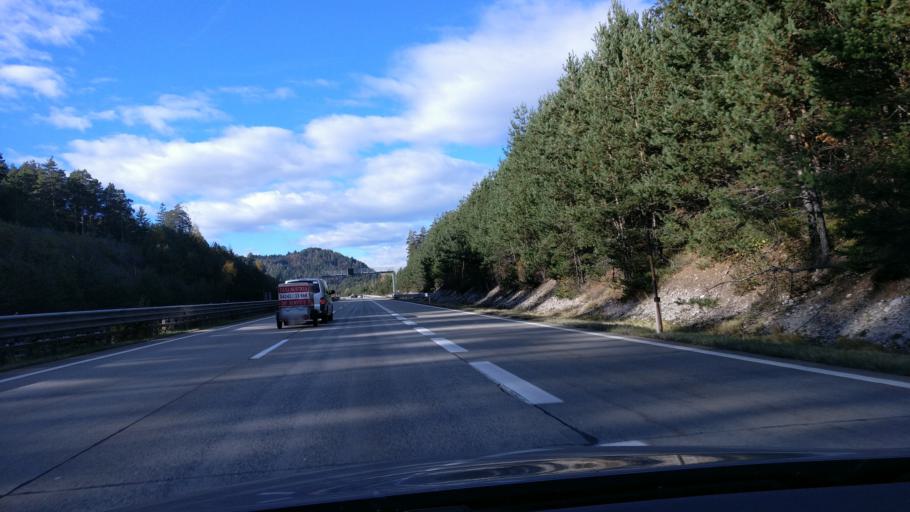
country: AT
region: Carinthia
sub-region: Politischer Bezirk Villach Land
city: Fresach
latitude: 46.6552
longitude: 13.7378
